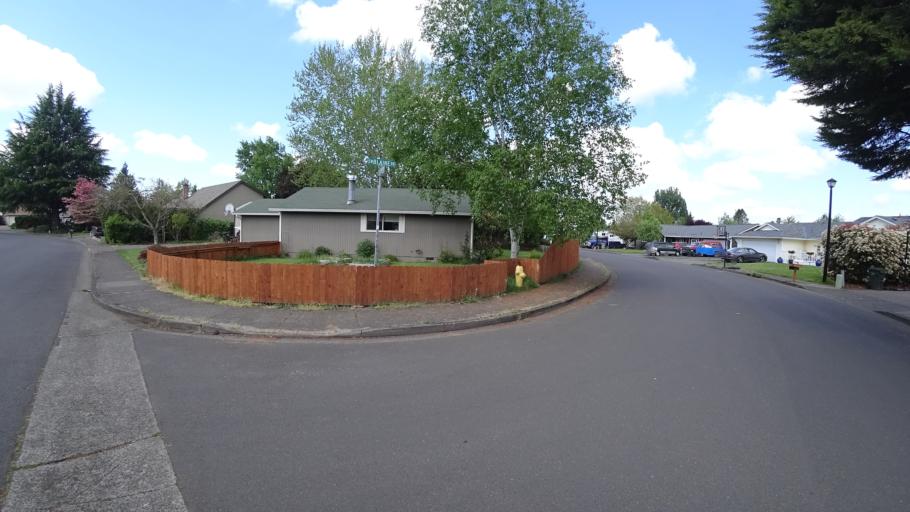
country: US
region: Oregon
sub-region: Washington County
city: Aloha
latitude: 45.5059
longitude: -122.8892
